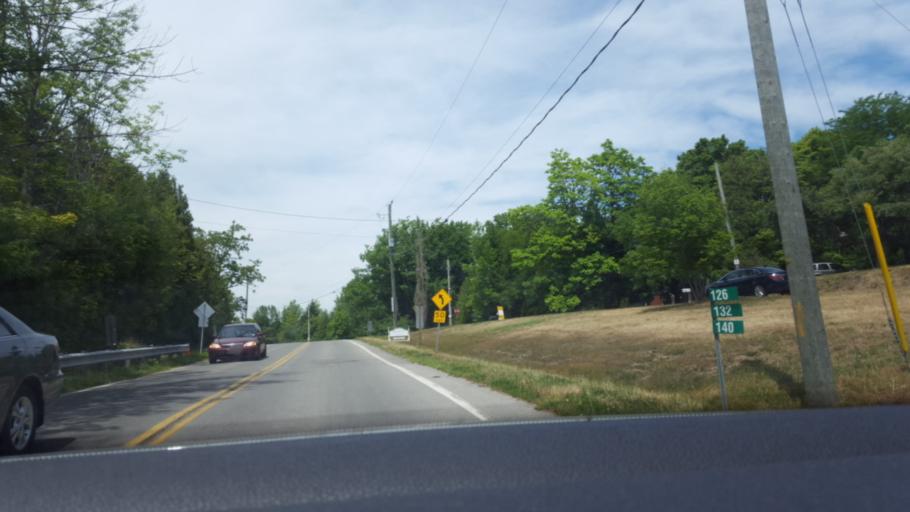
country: CA
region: Ontario
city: Hamilton
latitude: 43.1835
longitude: -79.5743
